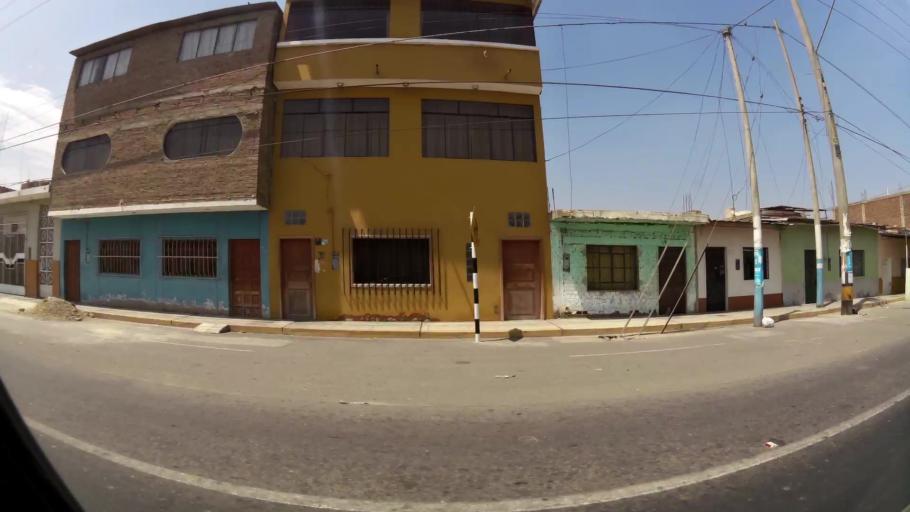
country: PE
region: La Libertad
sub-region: Chepen
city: Chepen
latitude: -7.2097
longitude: -79.4273
